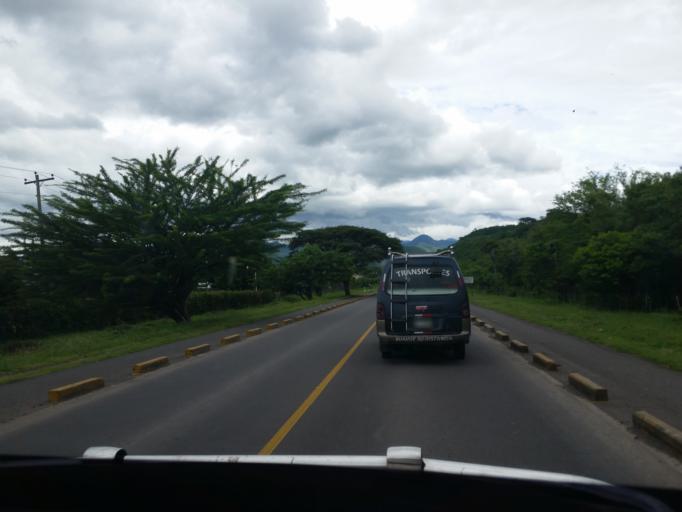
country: NI
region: Matagalpa
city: Ciudad Dario
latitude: 12.8718
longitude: -86.0882
